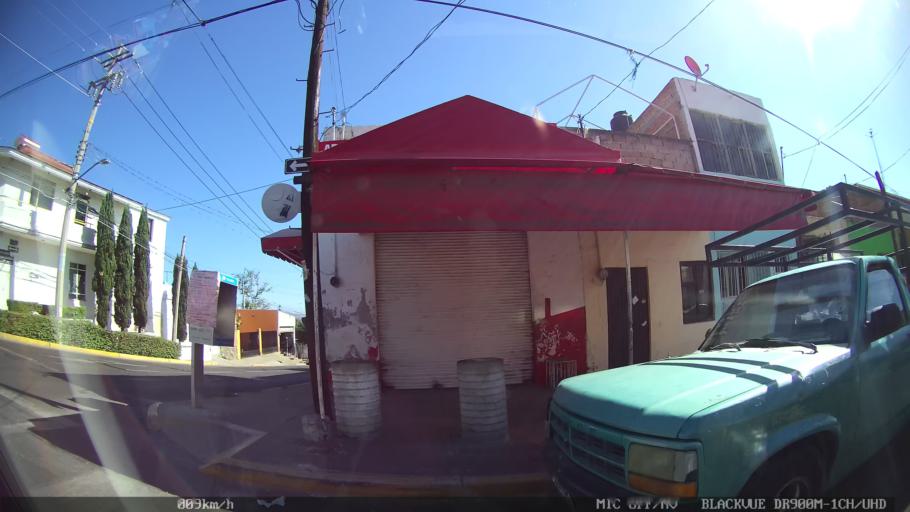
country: MX
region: Jalisco
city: Tlaquepaque
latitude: 20.6850
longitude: -103.2720
